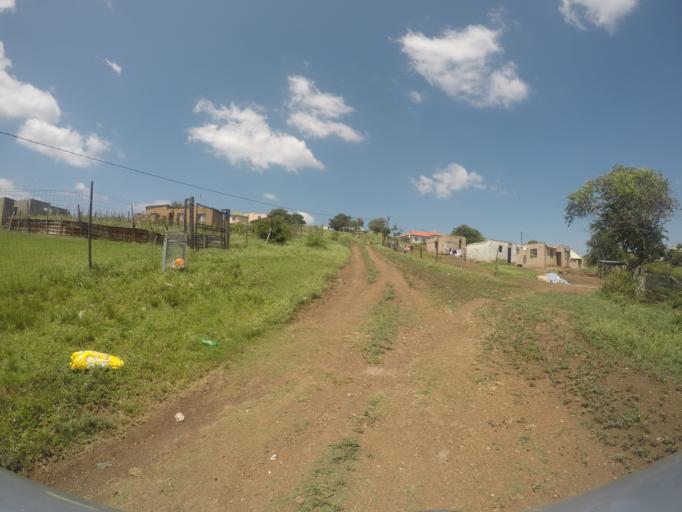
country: ZA
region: KwaZulu-Natal
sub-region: uThungulu District Municipality
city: Empangeni
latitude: -28.6080
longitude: 31.7358
